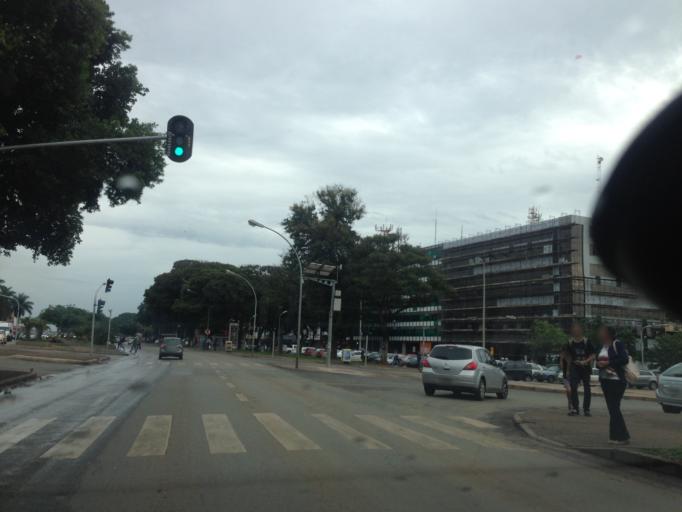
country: BR
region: Federal District
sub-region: Brasilia
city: Brasilia
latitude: -15.7980
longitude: -47.8919
